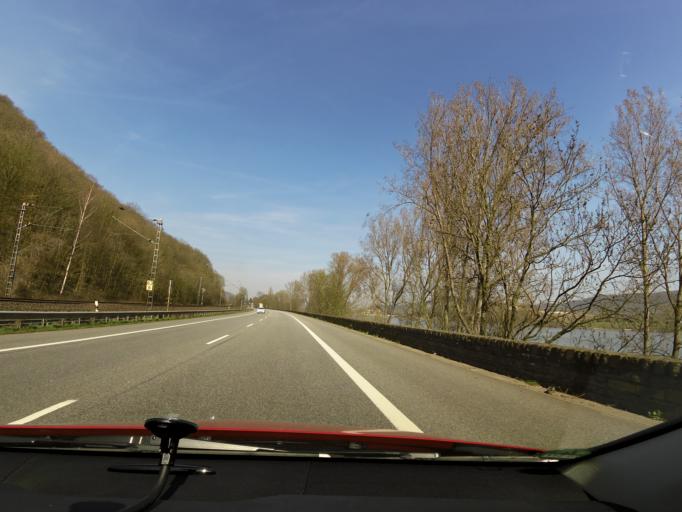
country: DE
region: Rheinland-Pfalz
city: Rheinbrohl
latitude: 50.4967
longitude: 7.3161
